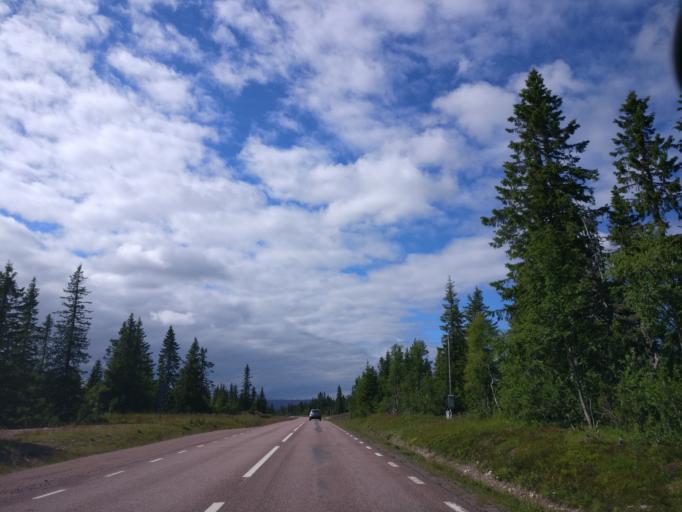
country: SE
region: Dalarna
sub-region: Malung-Saelens kommun
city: Malung
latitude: 61.1641
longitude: 13.1035
